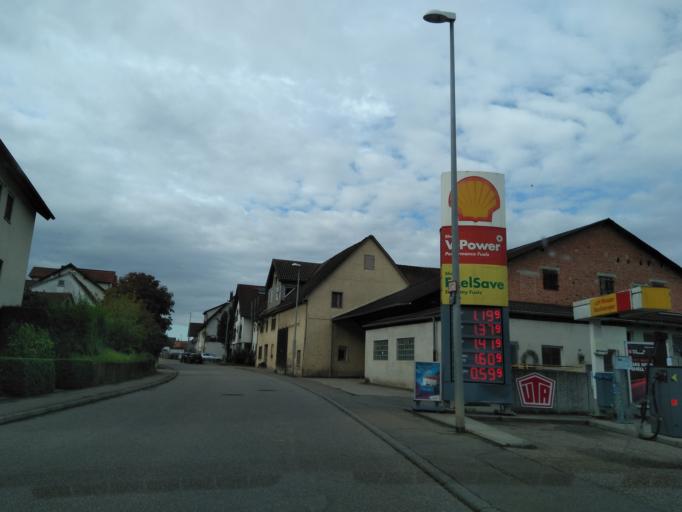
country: DE
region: Baden-Wuerttemberg
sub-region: Regierungsbezirk Stuttgart
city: Oberriexingen
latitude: 48.9377
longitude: 9.0531
